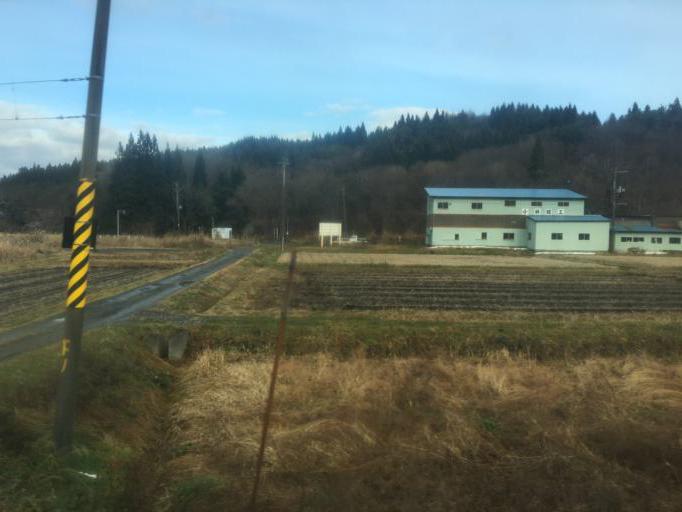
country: JP
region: Akita
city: Takanosu
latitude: 40.2629
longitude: 140.4283
